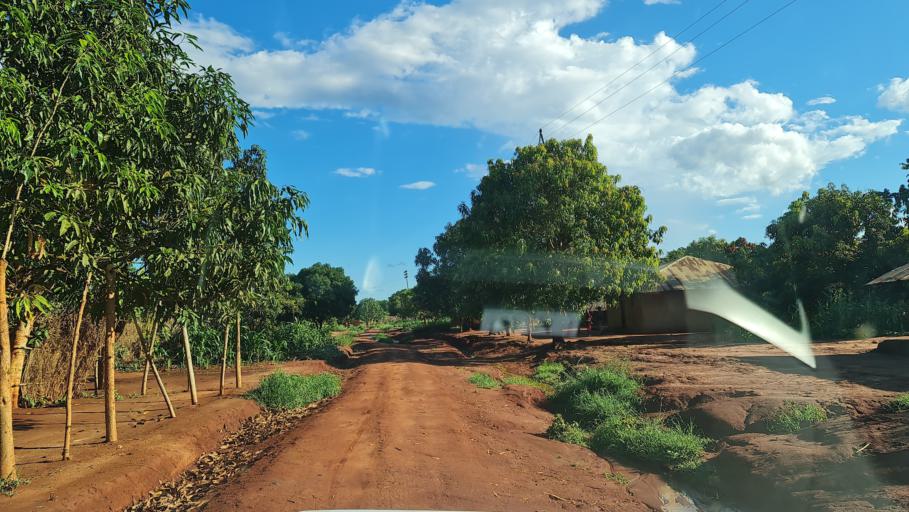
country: MZ
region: Nampula
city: Ilha de Mocambique
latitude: -14.9211
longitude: 40.2180
